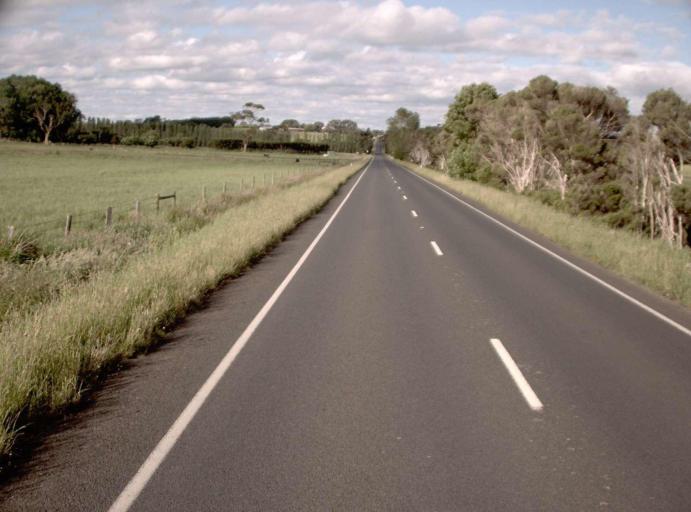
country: AU
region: Victoria
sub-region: Baw Baw
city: Warragul
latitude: -38.4939
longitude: 145.9267
